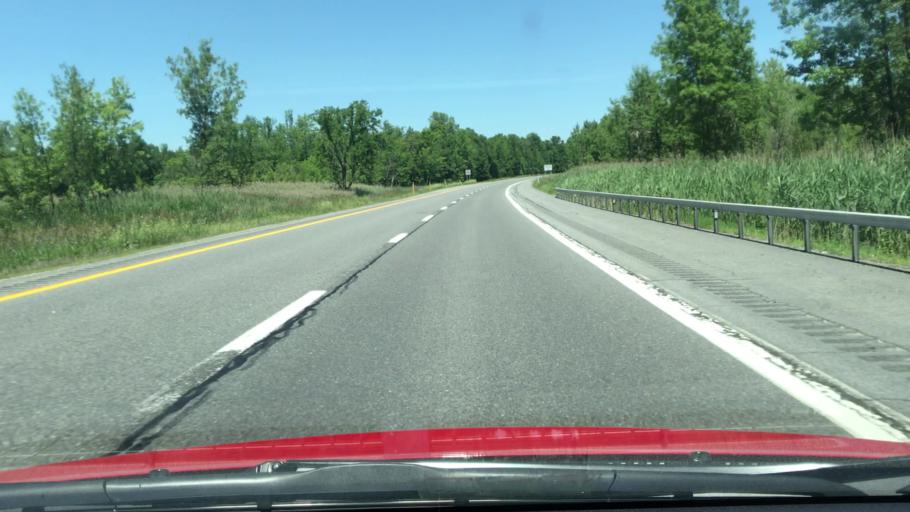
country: US
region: New York
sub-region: Clinton County
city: Champlain
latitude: 44.8969
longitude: -73.4546
